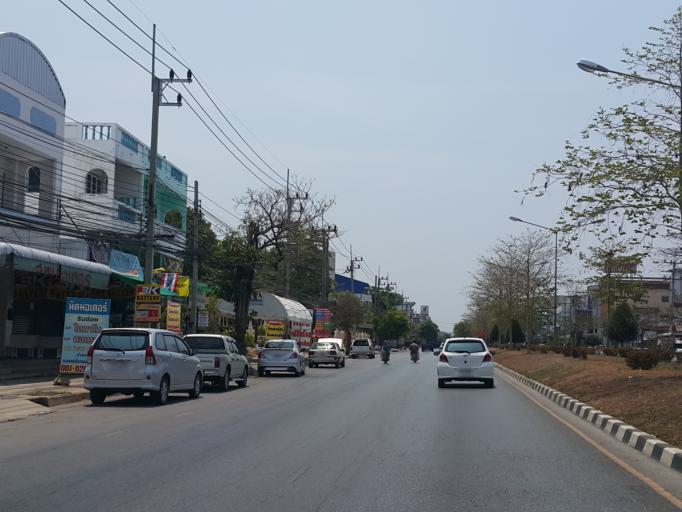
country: TH
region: Kanchanaburi
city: Kanchanaburi
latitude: 14.0414
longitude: 99.5152
